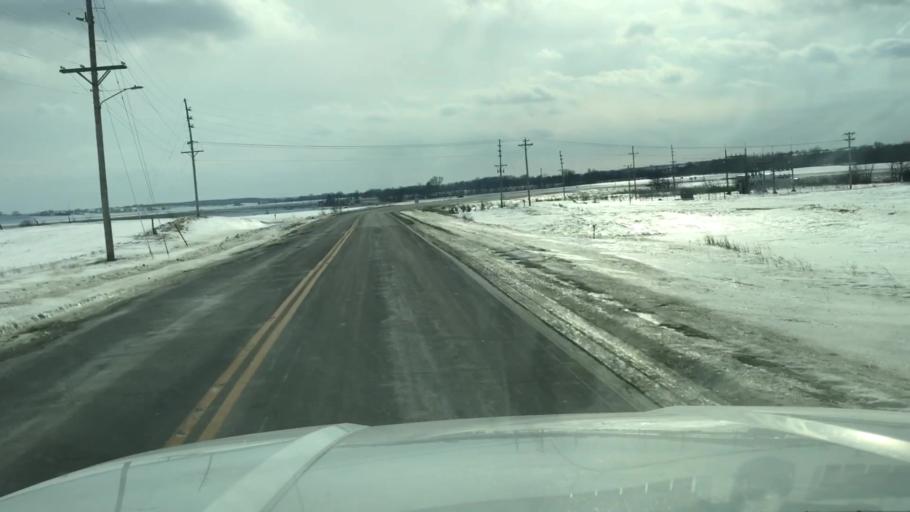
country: US
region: Missouri
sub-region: Gentry County
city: Stanberry
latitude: 40.3442
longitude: -94.6737
